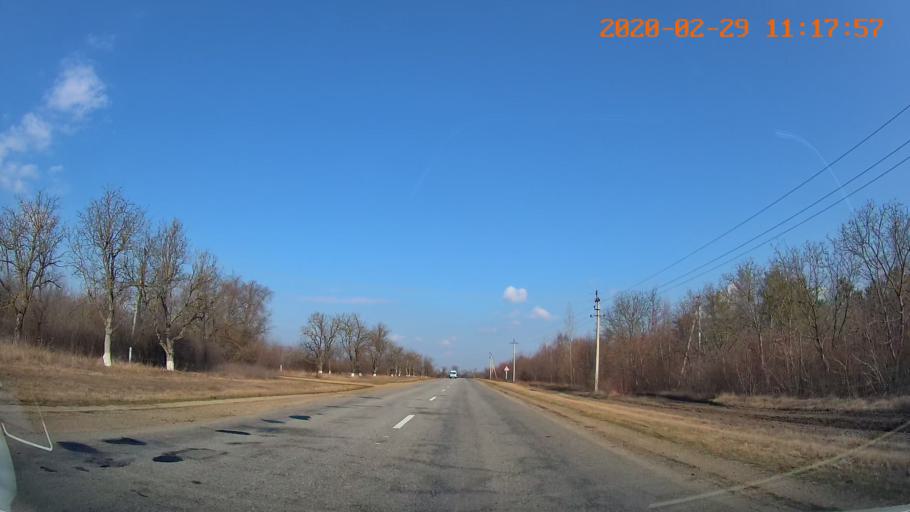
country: MD
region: Telenesti
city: Dubasari
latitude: 47.3283
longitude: 29.1717
